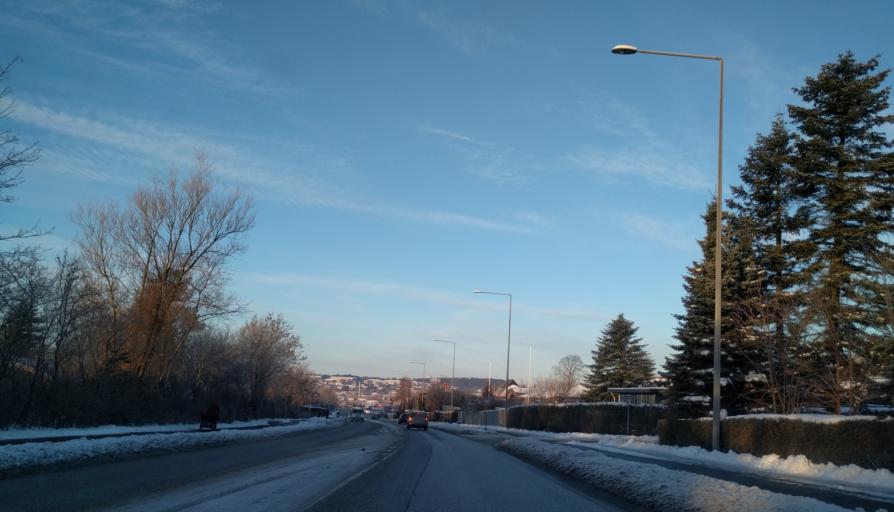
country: DK
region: North Denmark
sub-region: Alborg Kommune
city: Aalborg
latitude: 57.0262
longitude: 9.9358
